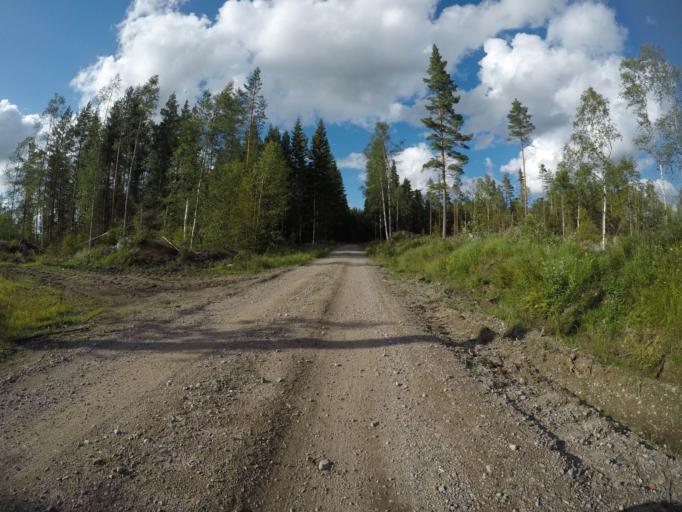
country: SE
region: OErebro
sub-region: Hallefors Kommun
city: Haellefors
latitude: 59.9180
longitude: 14.5572
